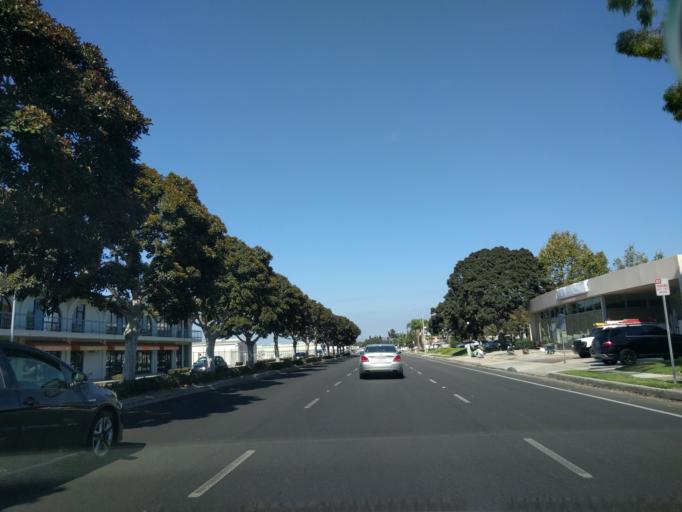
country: US
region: California
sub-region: Orange County
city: Irvine
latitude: 33.6660
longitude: -117.8714
